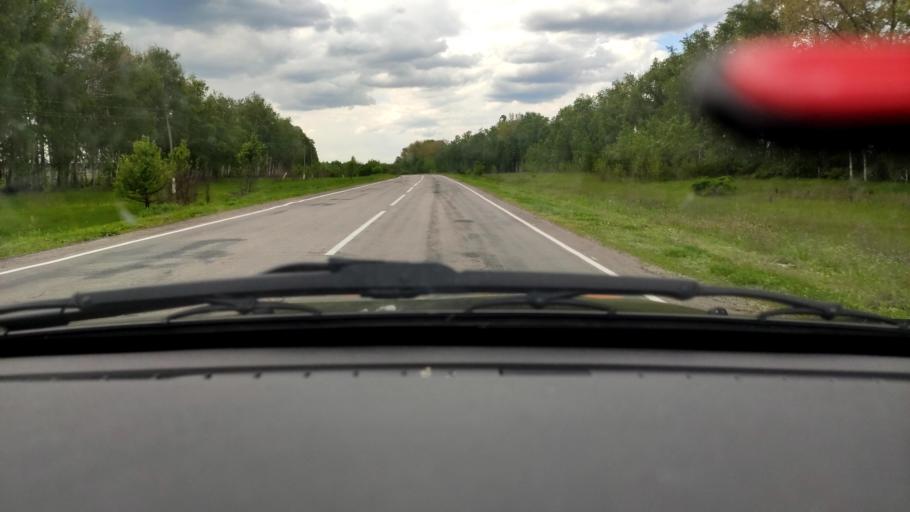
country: RU
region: Belgorod
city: Krasnoye
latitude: 51.0564
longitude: 38.8993
